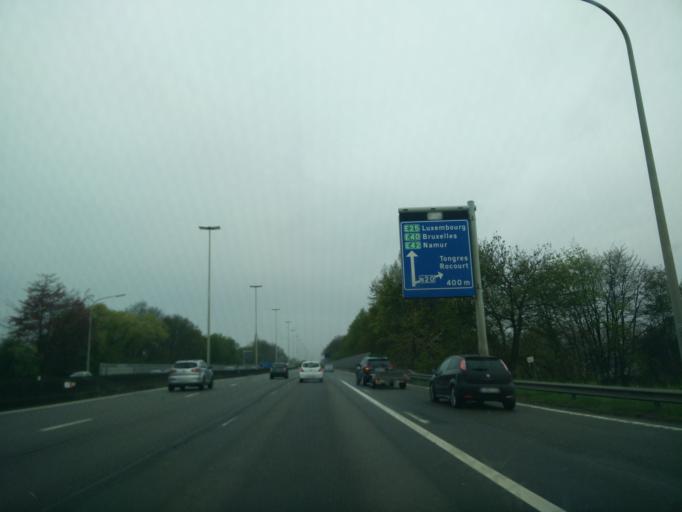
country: BE
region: Wallonia
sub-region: Province de Liege
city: Liege
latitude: 50.6746
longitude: 5.5639
